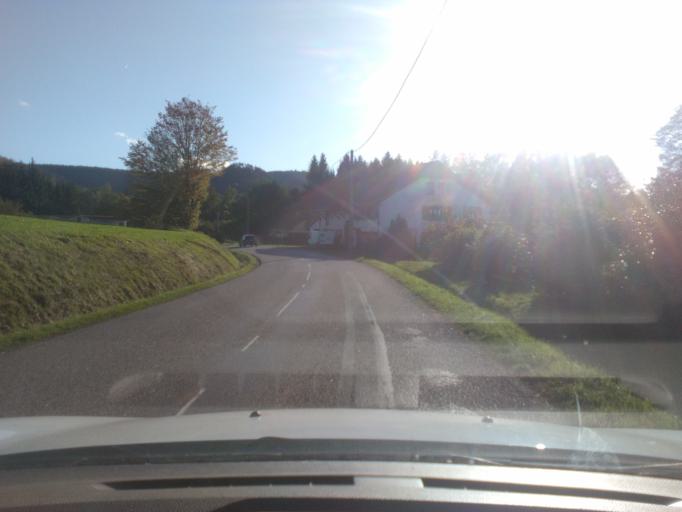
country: FR
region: Lorraine
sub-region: Departement des Vosges
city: Saint-Michel-sur-Meurthe
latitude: 48.3167
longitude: 6.8426
